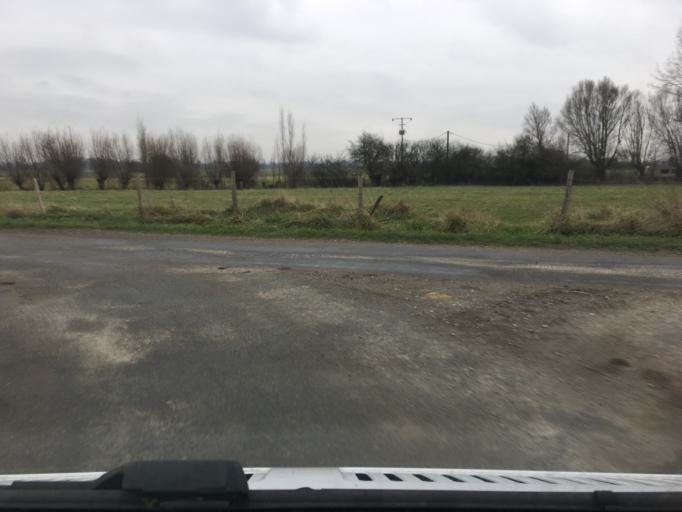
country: FR
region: Picardie
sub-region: Departement de la Somme
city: Pende
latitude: 50.1867
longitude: 1.5477
